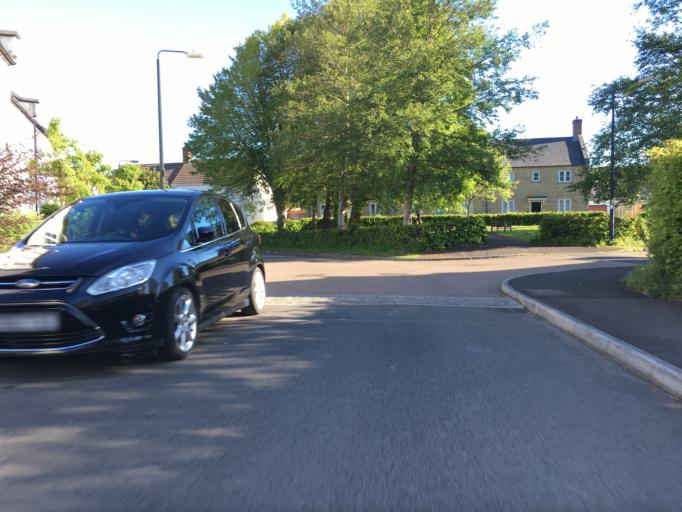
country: GB
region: England
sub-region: North Somerset
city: Long Ashton
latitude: 51.4235
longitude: -2.6957
